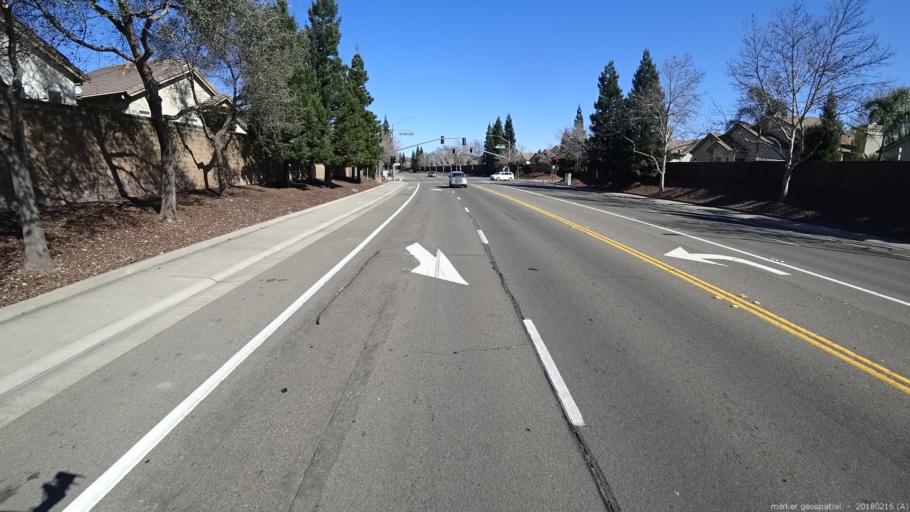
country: US
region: California
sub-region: Sacramento County
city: Gold River
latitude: 38.6297
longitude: -121.2263
